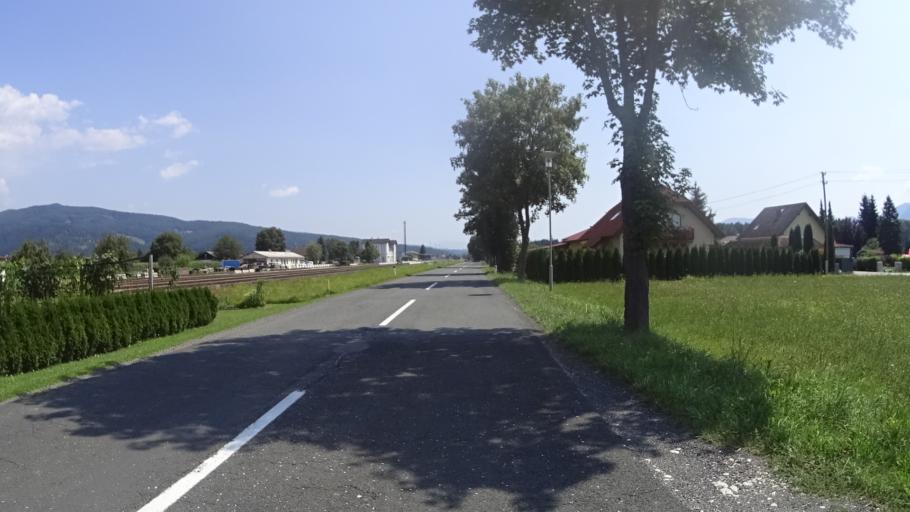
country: AT
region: Carinthia
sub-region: Politischer Bezirk Volkermarkt
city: Bleiburg/Pliberk
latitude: 46.5746
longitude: 14.7822
